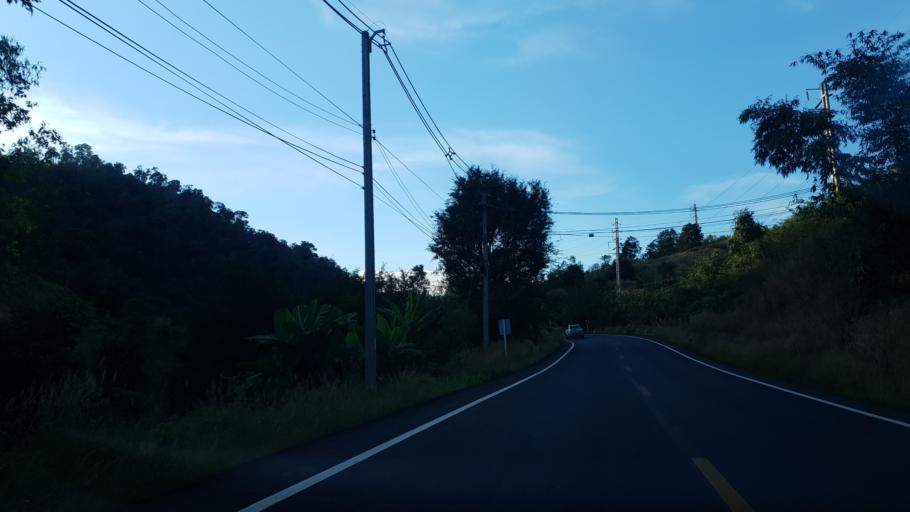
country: TH
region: Loei
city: Dan Sai
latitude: 17.2265
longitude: 101.0602
